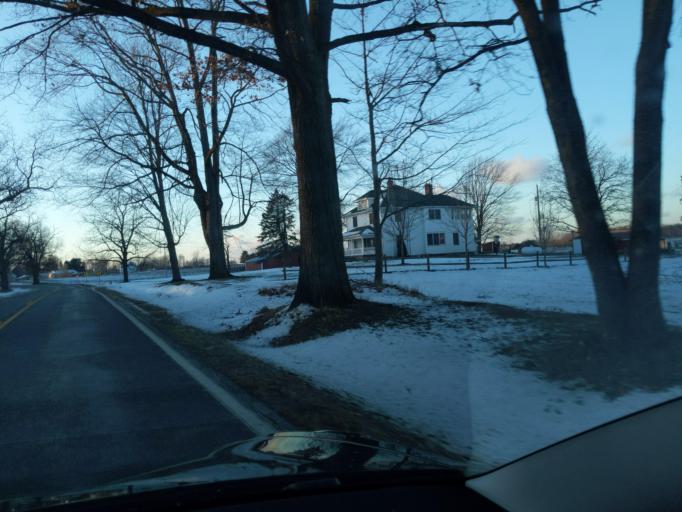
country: US
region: Michigan
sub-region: Ingham County
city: Stockbridge
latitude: 42.4498
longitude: -84.2524
